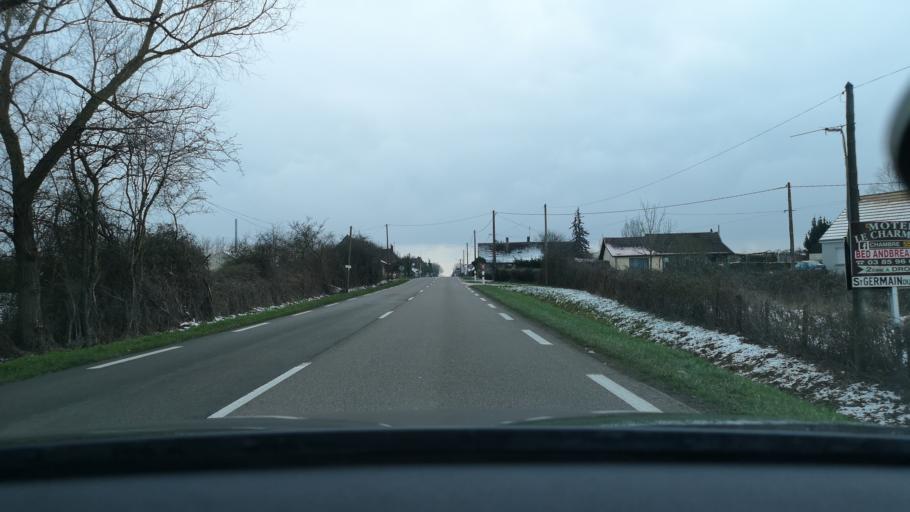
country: FR
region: Bourgogne
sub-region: Departement de Saone-et-Loire
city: Saint-Germain-du-Plain
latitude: 46.7543
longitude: 5.0184
